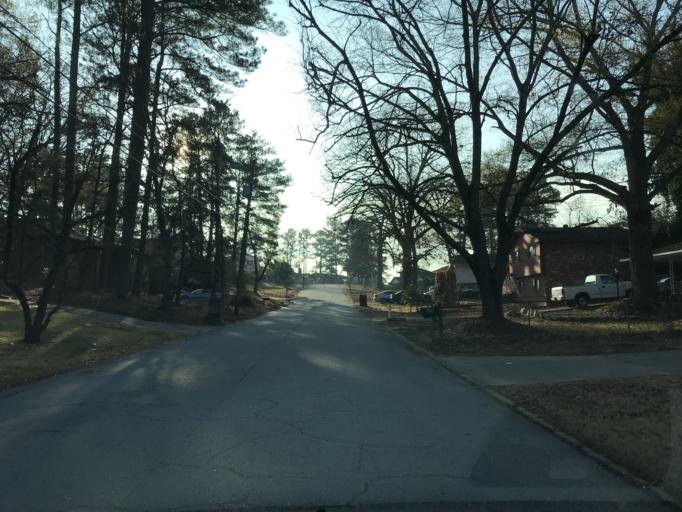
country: US
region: Georgia
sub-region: Fulton County
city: College Park
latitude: 33.6137
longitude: -84.4305
